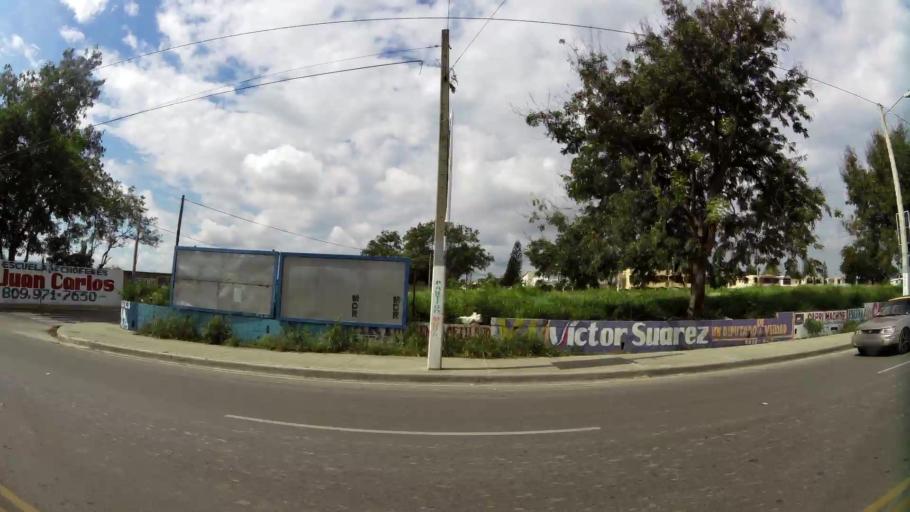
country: DO
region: Santiago
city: Santiago de los Caballeros
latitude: 19.4754
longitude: -70.7225
